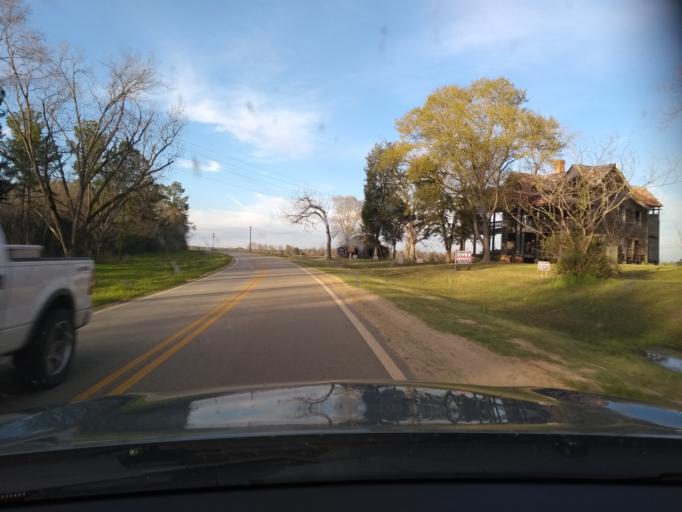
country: US
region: Georgia
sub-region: Bulloch County
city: Statesboro
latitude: 32.3232
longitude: -81.7758
